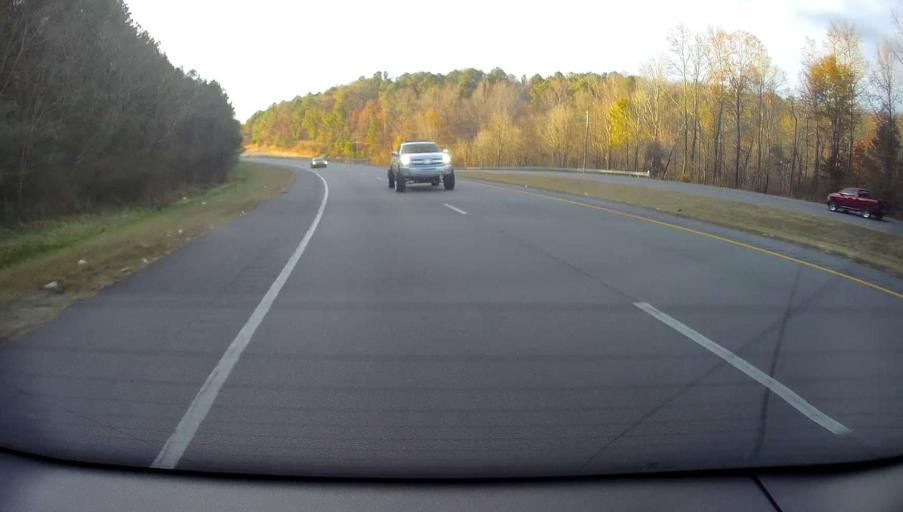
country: US
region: Alabama
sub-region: Blount County
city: Blountsville
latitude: 34.1626
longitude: -86.5019
